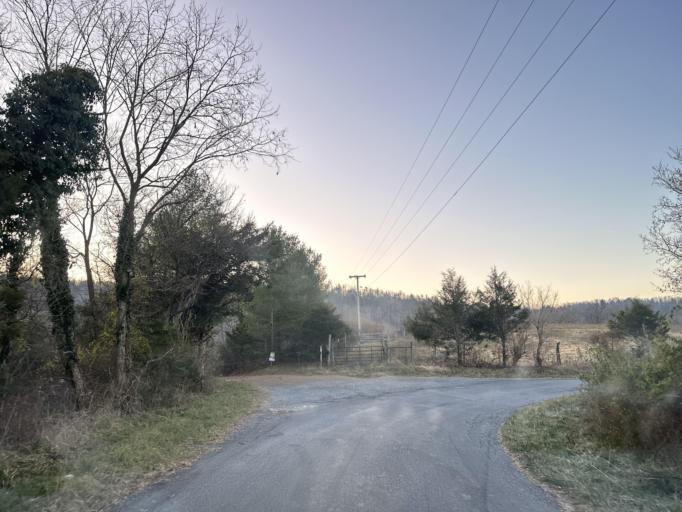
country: US
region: Virginia
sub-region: Augusta County
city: Jolivue
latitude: 38.0810
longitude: -79.3652
